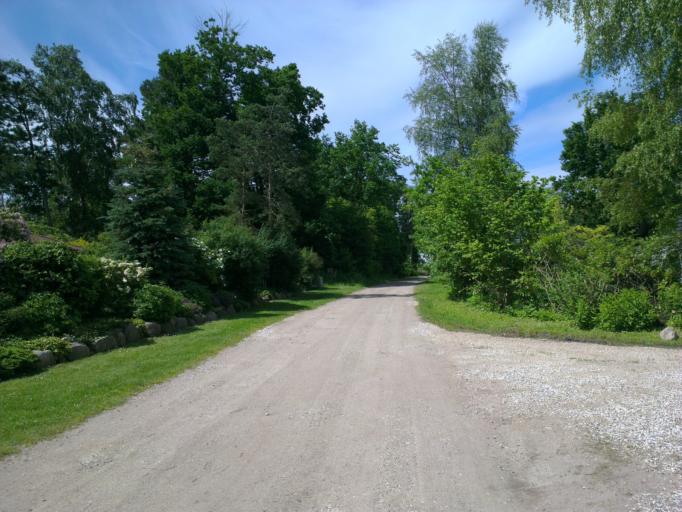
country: DK
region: Capital Region
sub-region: Frederikssund Kommune
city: Jaegerspris
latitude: 55.8200
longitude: 11.9422
